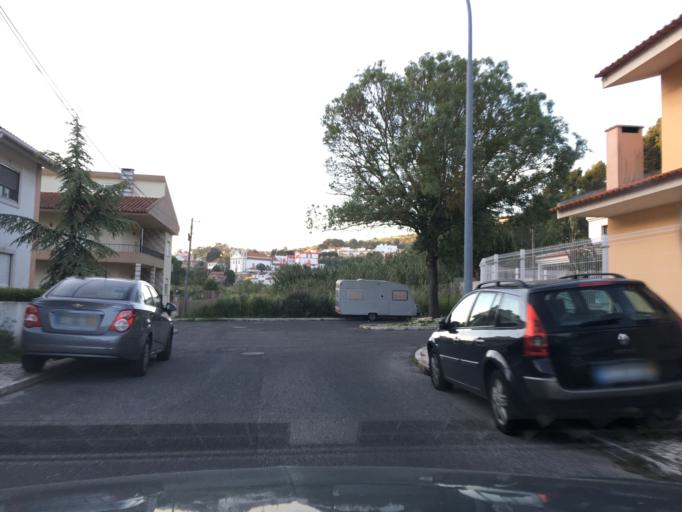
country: PT
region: Lisbon
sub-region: Oeiras
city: Barcarena
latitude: 38.7279
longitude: -9.2771
